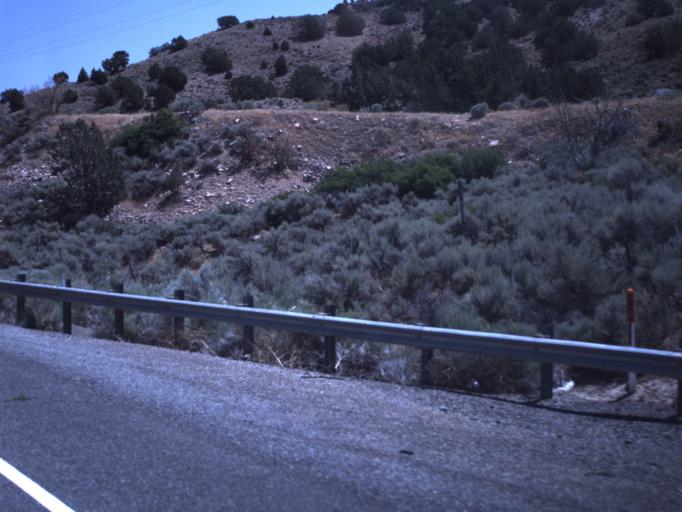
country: US
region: Utah
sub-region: Juab County
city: Nephi
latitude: 39.5558
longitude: -112.2138
